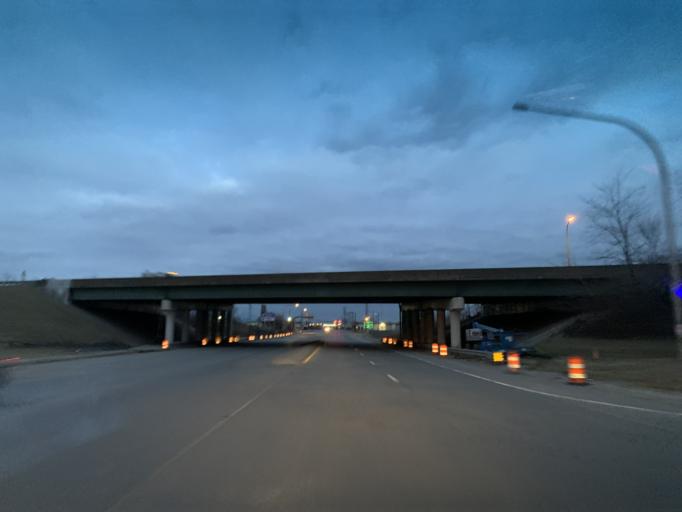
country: US
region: Delaware
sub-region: New Castle County
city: Wilmington
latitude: 39.7202
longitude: -75.5414
